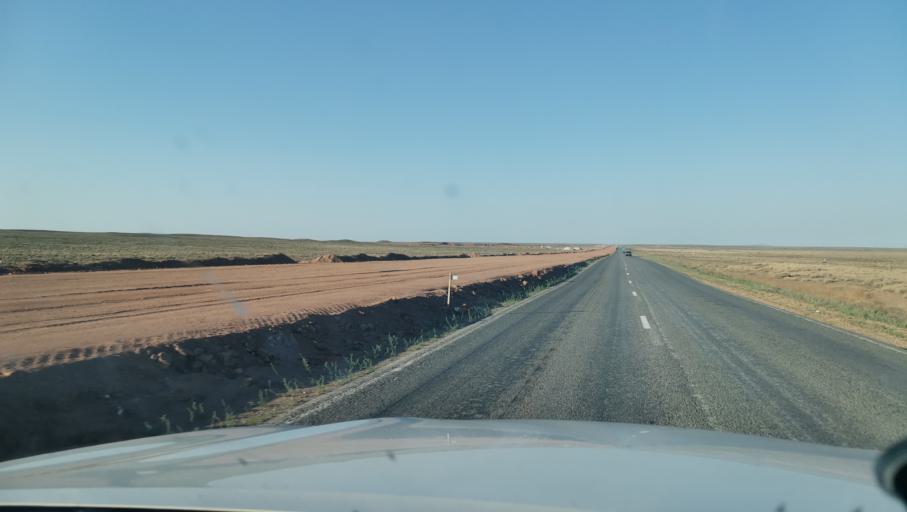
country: KZ
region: Qaraghandy
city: Saryshaghan
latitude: 46.4598
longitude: 74.0120
